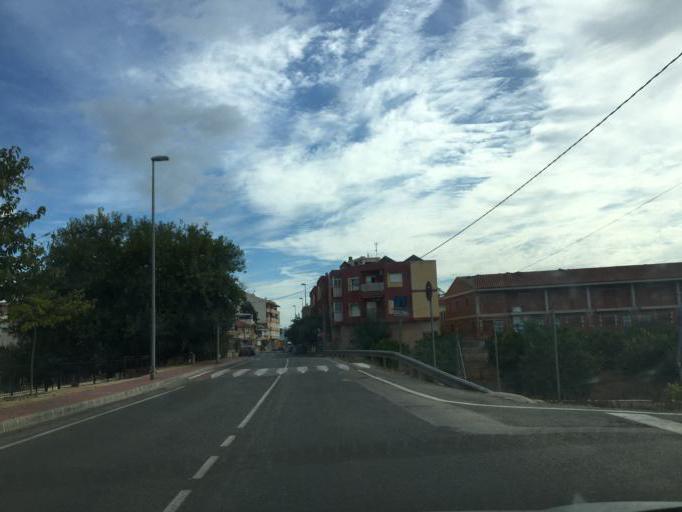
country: ES
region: Murcia
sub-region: Murcia
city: Beniel
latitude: 38.0117
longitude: -1.0366
